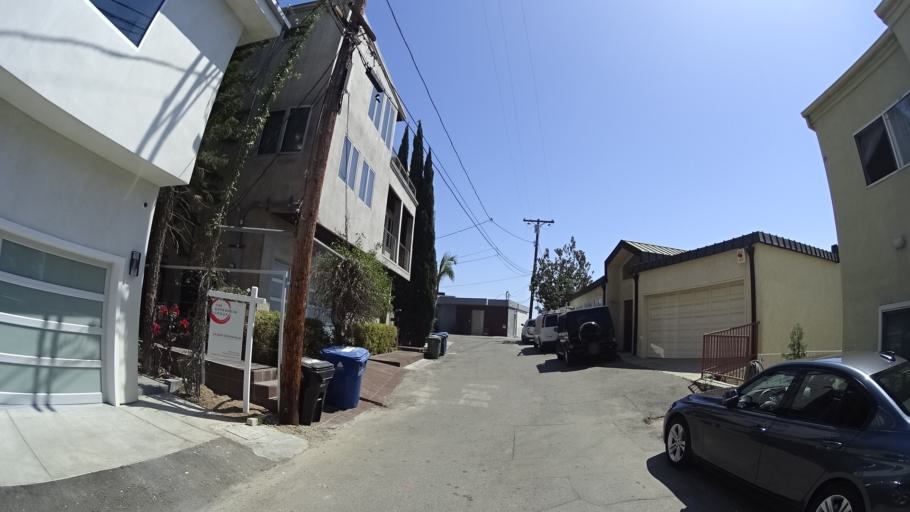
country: US
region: California
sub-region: Los Angeles County
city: West Hollywood
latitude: 34.1006
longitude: -118.3792
